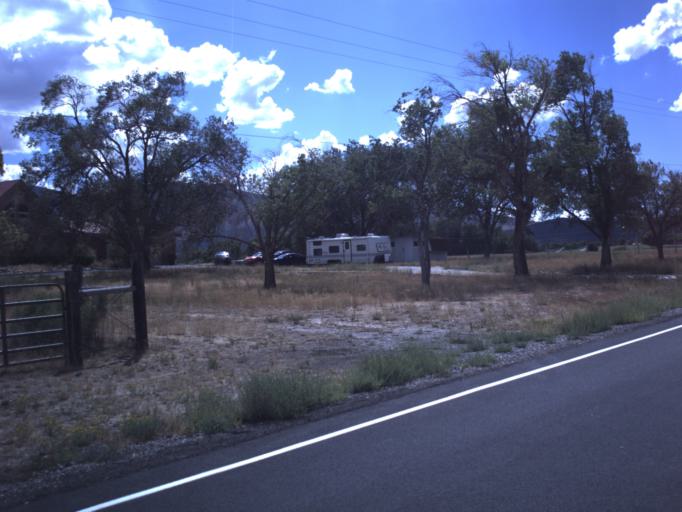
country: US
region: Utah
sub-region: Tooele County
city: Tooele
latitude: 40.3384
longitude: -112.4757
